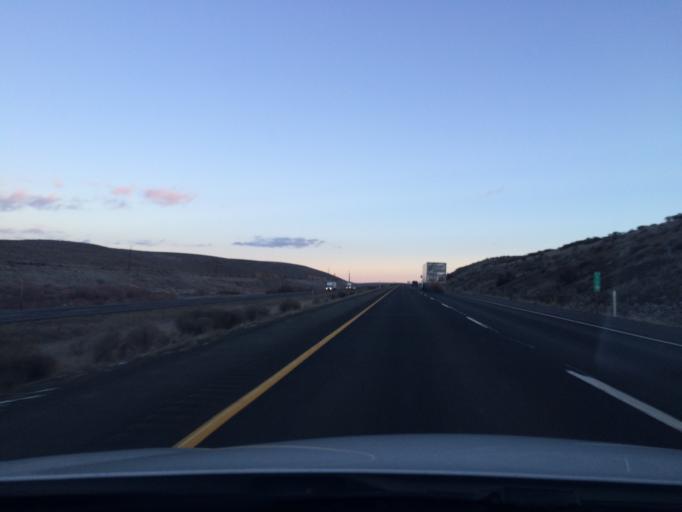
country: US
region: Washington
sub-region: Kittitas County
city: Kittitas
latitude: 46.9673
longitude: -120.3411
